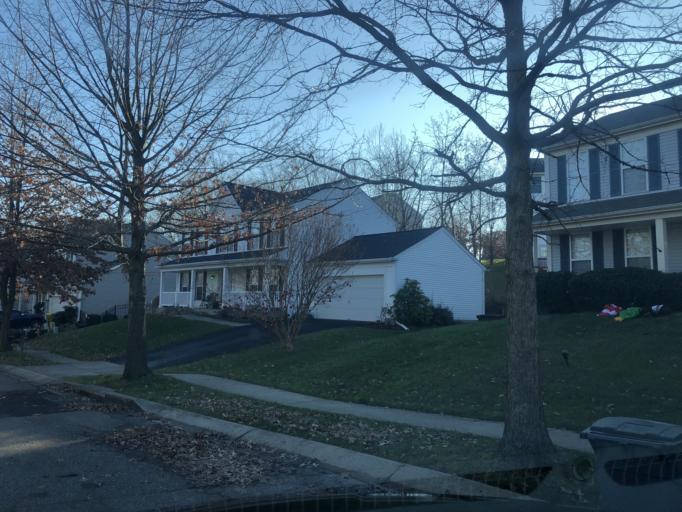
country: US
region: Maryland
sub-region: Anne Arundel County
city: Odenton
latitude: 39.0812
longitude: -76.7057
